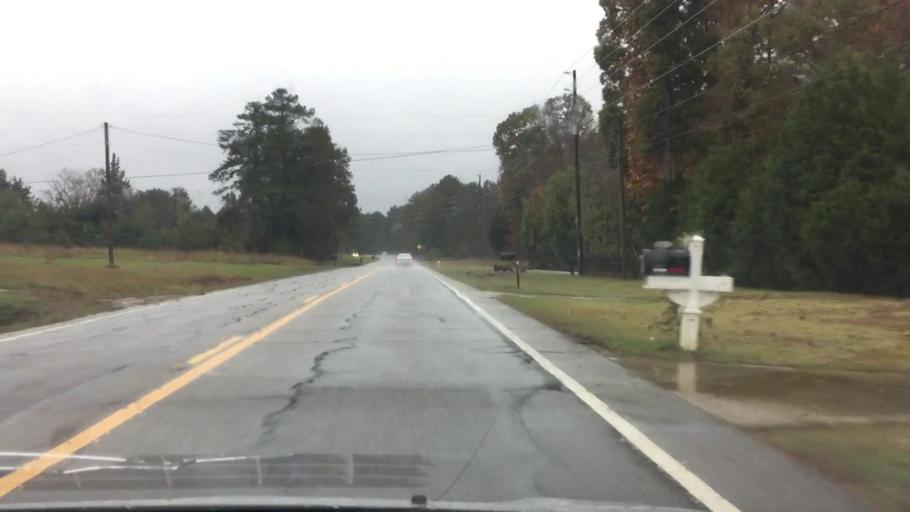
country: US
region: Georgia
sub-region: Henry County
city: Stockbridge
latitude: 33.5591
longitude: -84.1374
